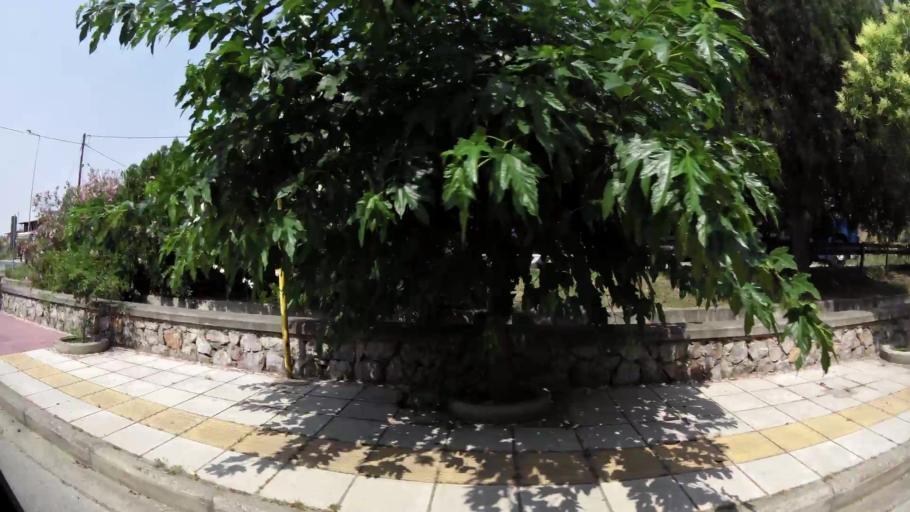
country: GR
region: Central Macedonia
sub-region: Nomos Thessalonikis
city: Diavata
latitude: 40.6900
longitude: 22.8601
